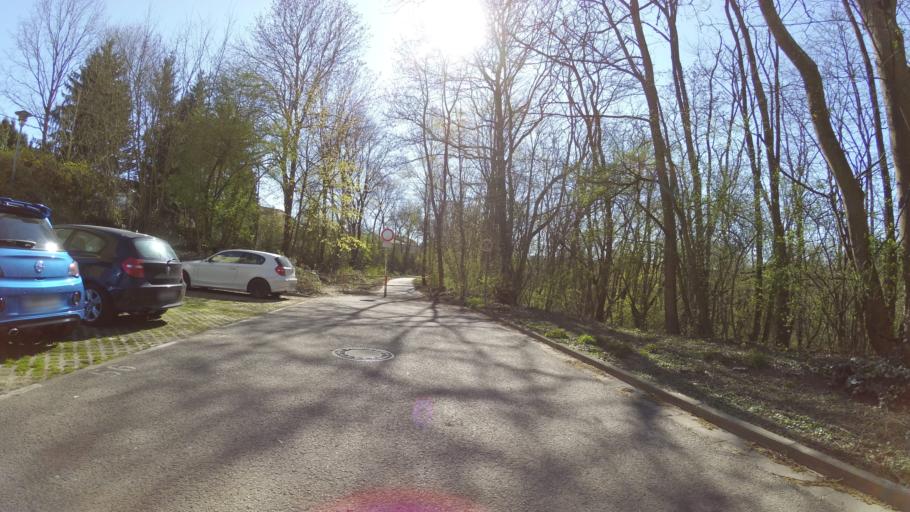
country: DE
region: Saarland
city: Volklingen
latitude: 49.2519
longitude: 6.8656
